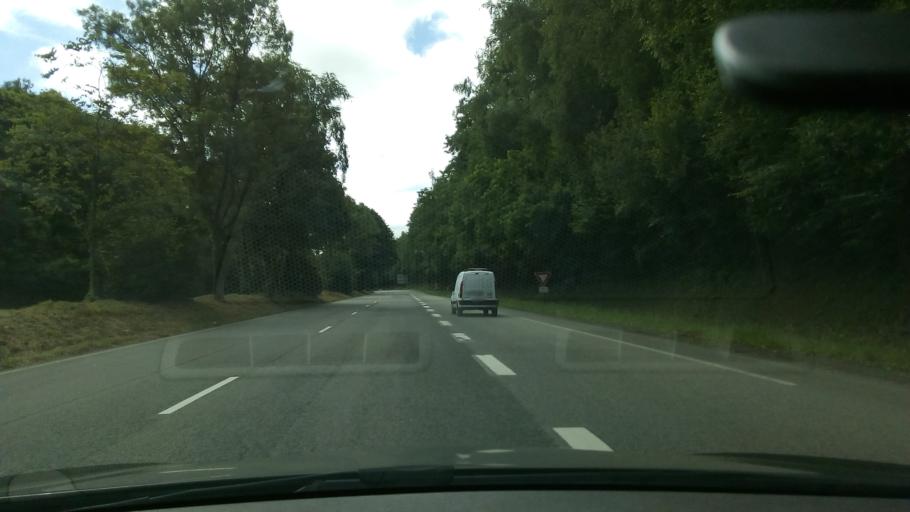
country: FR
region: Brittany
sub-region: Departement du Finistere
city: Quimper
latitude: 47.9824
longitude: -4.1105
